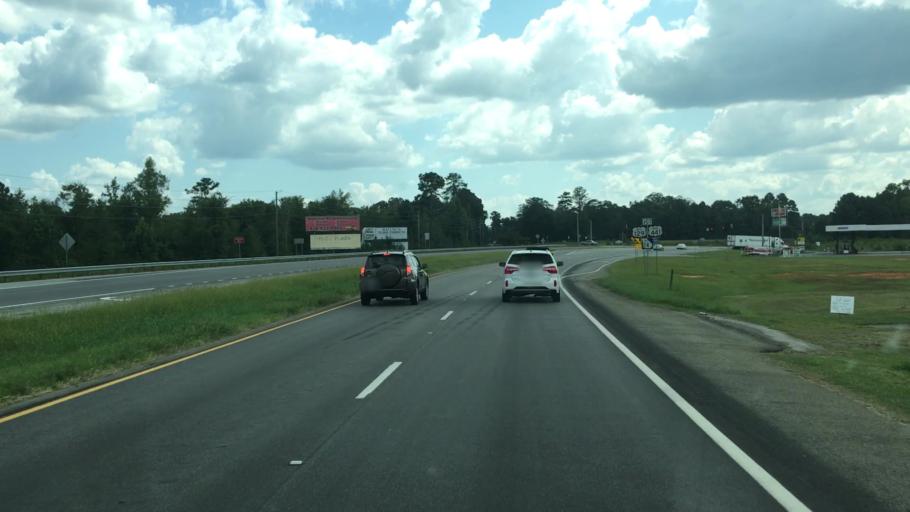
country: US
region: Georgia
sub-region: Putnam County
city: Eatonton
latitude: 33.3494
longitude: -83.3916
